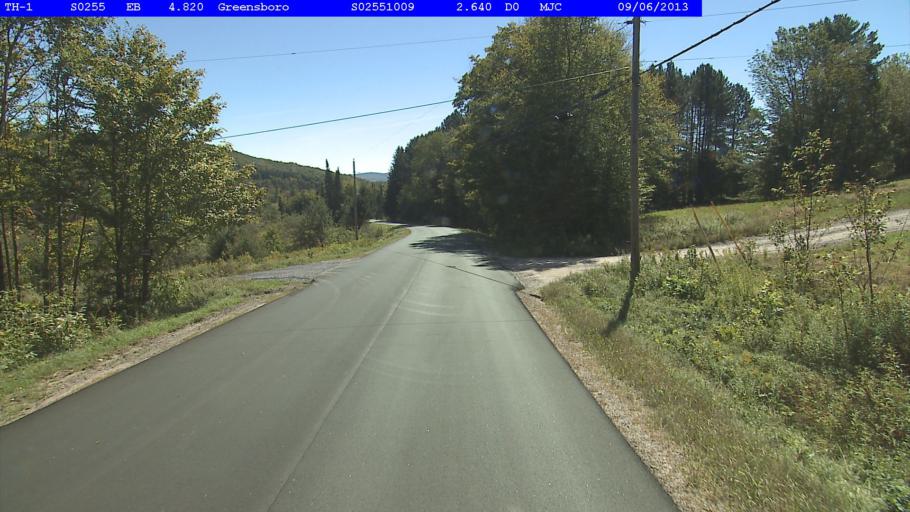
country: US
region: Vermont
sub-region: Caledonia County
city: Hardwick
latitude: 44.6058
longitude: -72.3157
